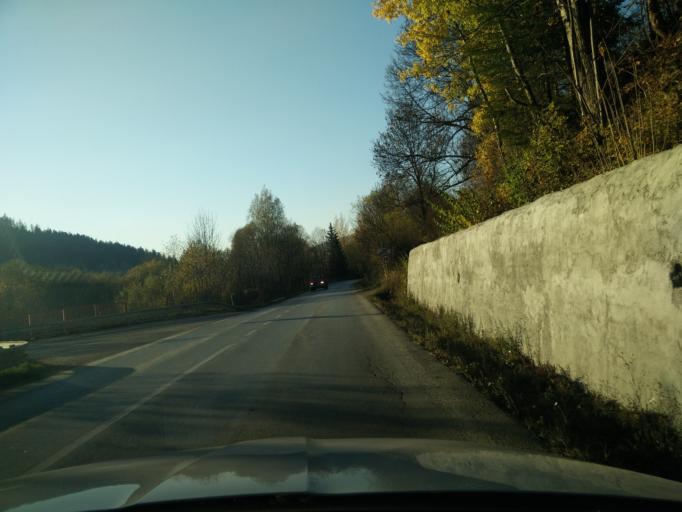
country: SK
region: Zilinsky
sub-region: Okres Zilina
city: Terchova
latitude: 49.3454
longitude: 18.9941
